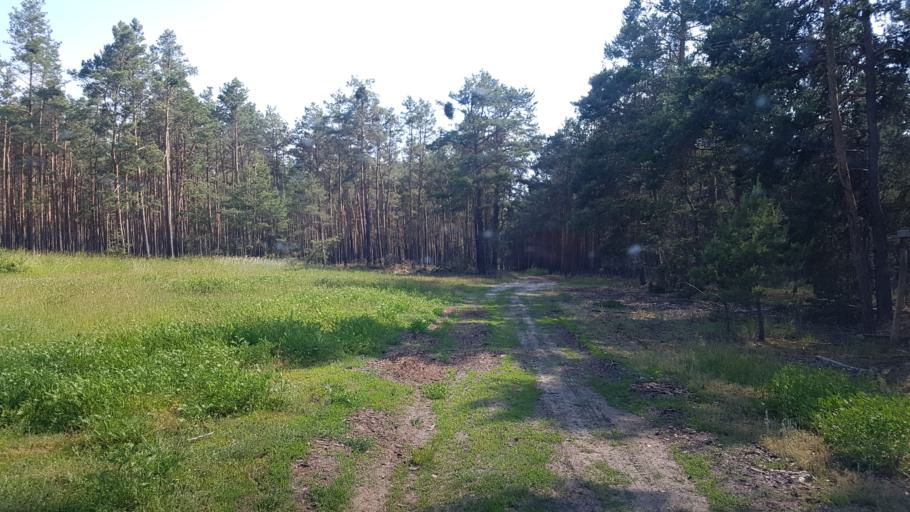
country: DE
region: Brandenburg
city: Trobitz
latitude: 51.6458
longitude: 13.4339
